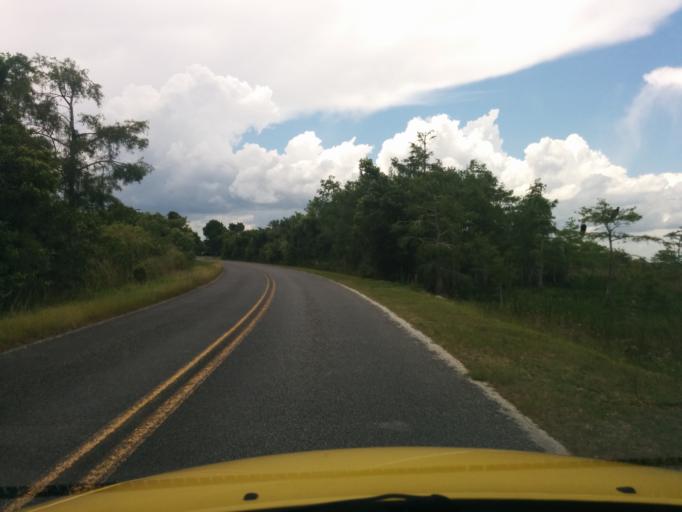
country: US
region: Florida
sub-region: Miami-Dade County
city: Florida City
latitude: 25.4391
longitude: -80.7819
